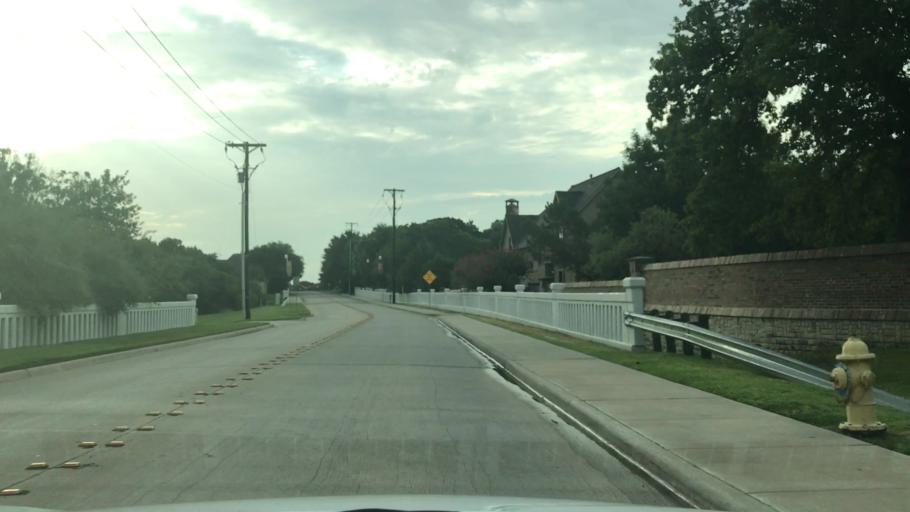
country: US
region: Texas
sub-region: Dallas County
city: Coppell
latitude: 32.9546
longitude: -96.9986
